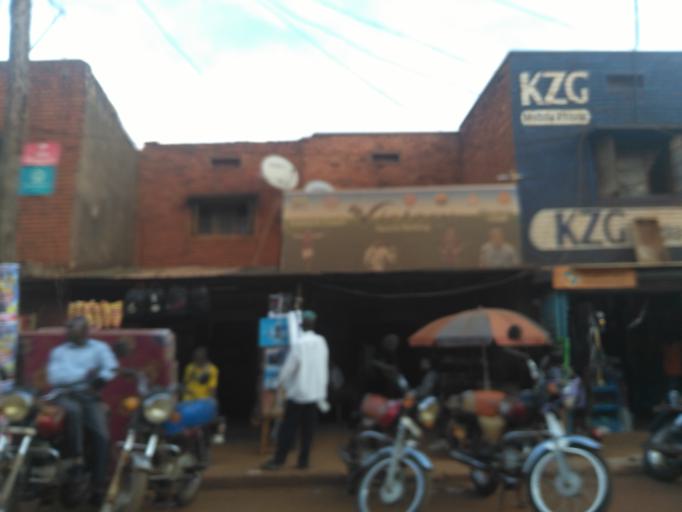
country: UG
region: Eastern Region
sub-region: Jinja District
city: Jinja
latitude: 0.4311
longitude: 33.2139
